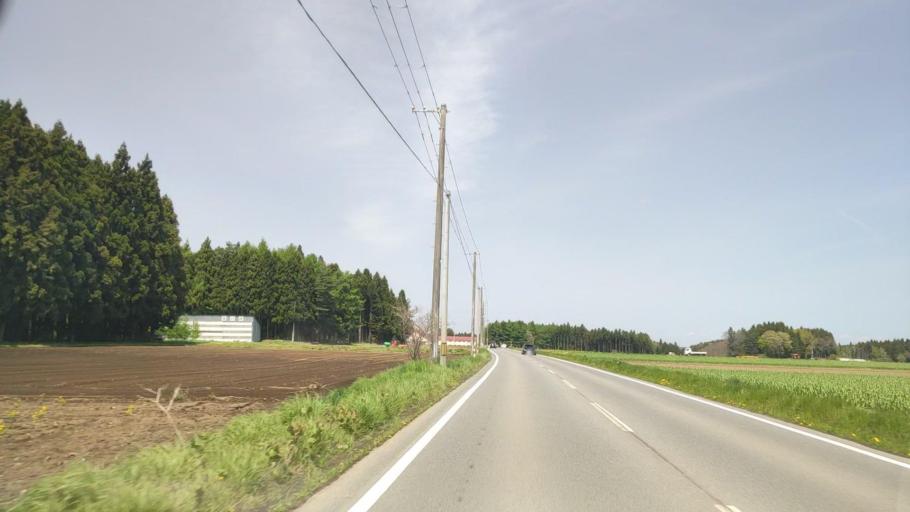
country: JP
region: Aomori
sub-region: Hachinohe Shi
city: Uchimaru
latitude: 40.5398
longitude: 141.4006
